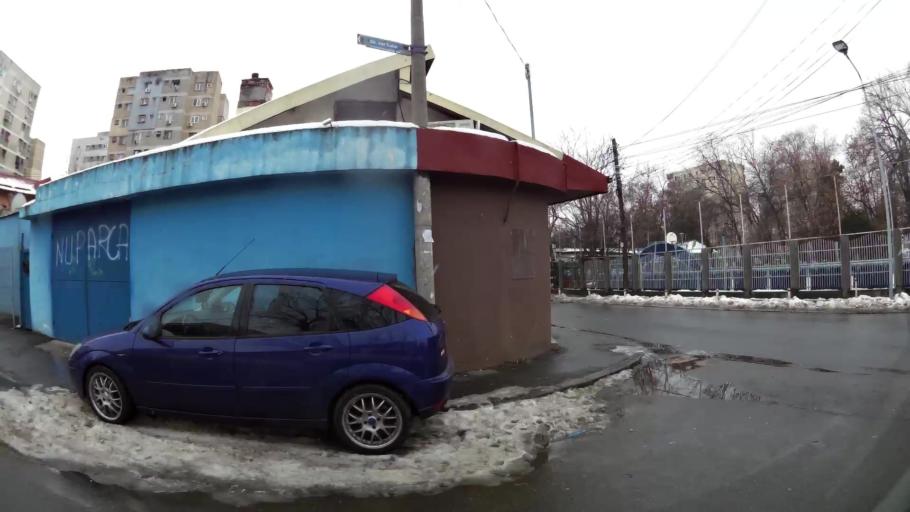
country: RO
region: Ilfov
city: Dobroesti
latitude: 44.4186
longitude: 26.1715
